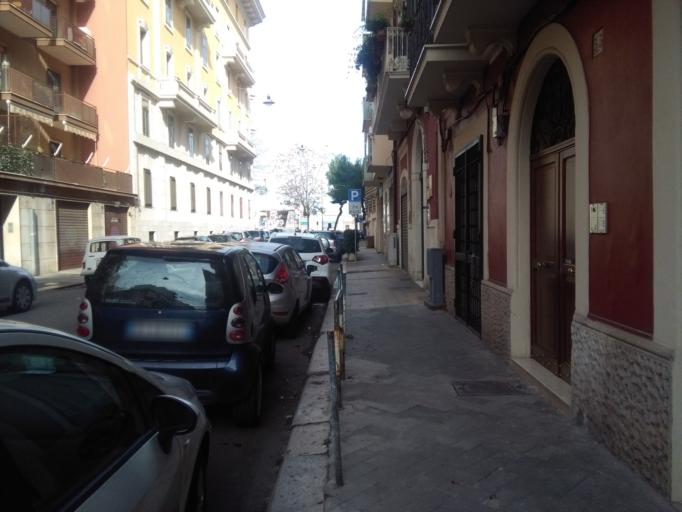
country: IT
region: Apulia
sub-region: Provincia di Bari
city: Bari
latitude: 41.1277
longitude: 16.8627
